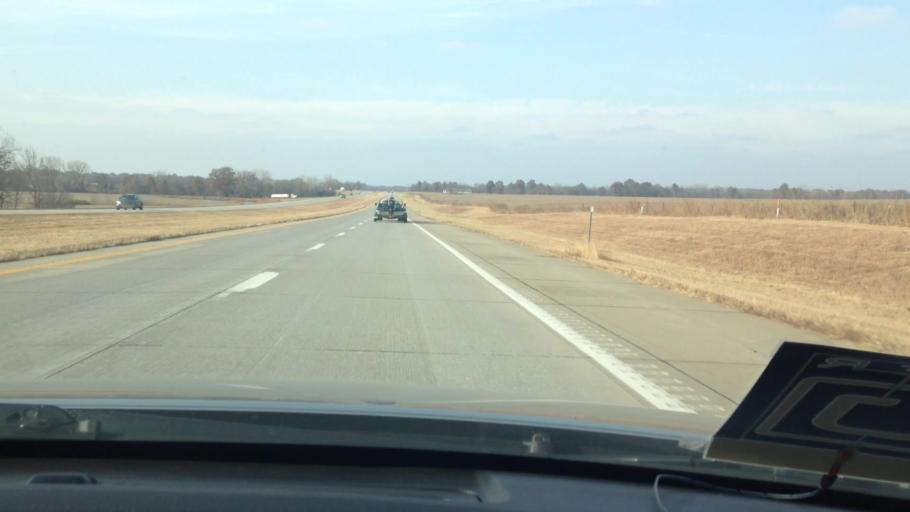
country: US
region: Missouri
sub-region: Henry County
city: Clinton
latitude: 38.4469
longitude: -93.9569
